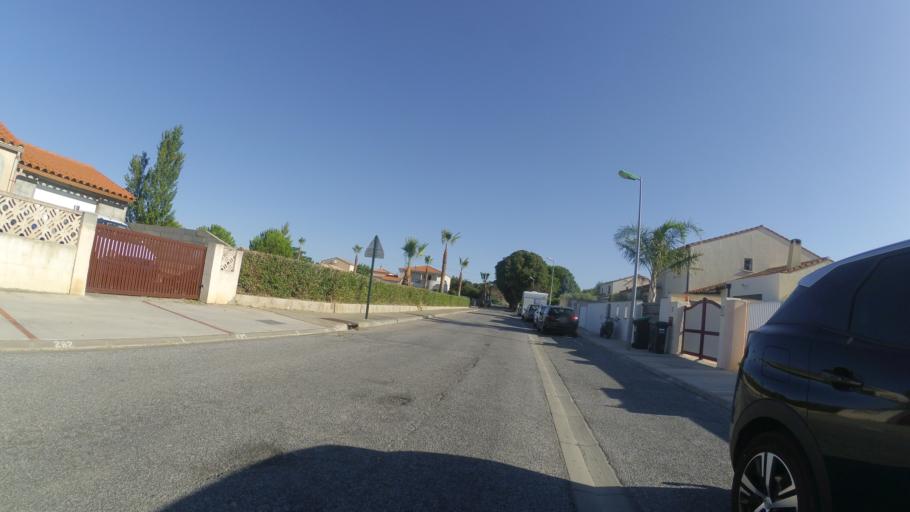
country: FR
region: Languedoc-Roussillon
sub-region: Departement des Pyrenees-Orientales
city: Baho
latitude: 42.7049
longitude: 2.8222
